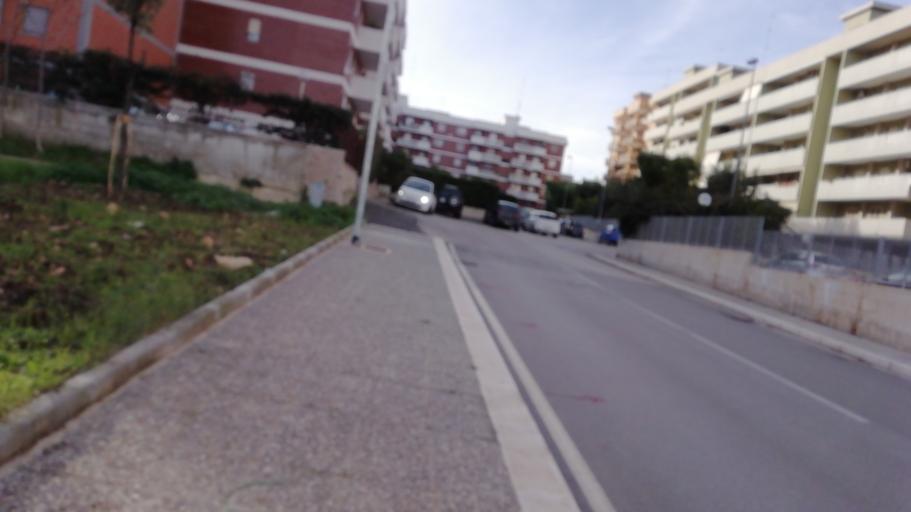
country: IT
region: Apulia
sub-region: Provincia di Bari
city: Triggiano
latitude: 41.1043
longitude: 16.9189
